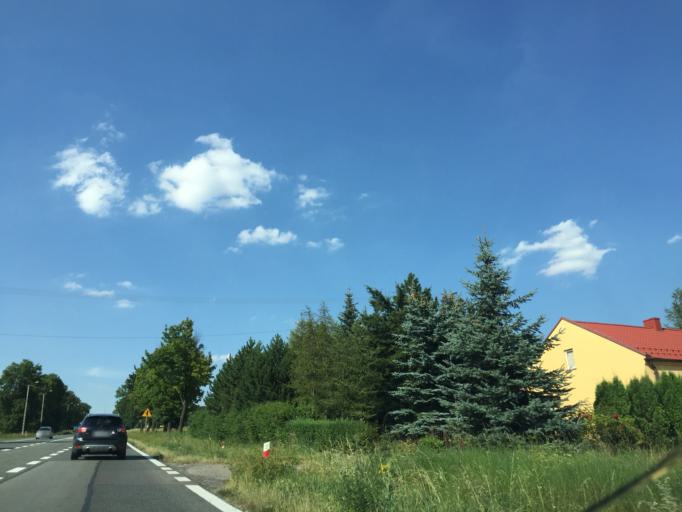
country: PL
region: Lesser Poland Voivodeship
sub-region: Powiat miechowski
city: Miechow
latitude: 50.3749
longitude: 20.0456
